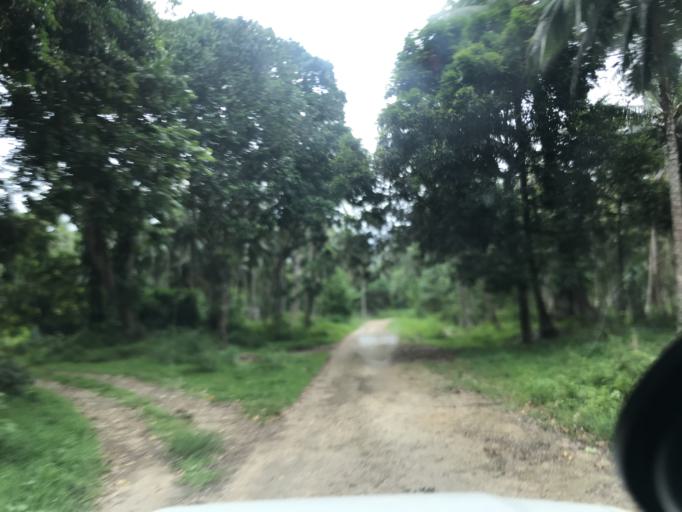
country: VU
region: Sanma
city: Port-Olry
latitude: -15.1674
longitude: 166.9484
